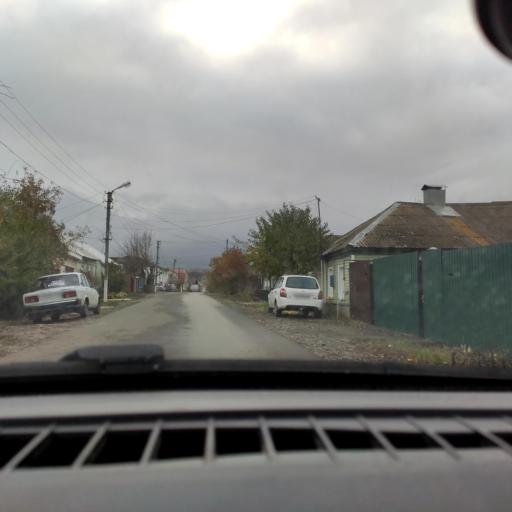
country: RU
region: Belgorod
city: Alekseyevka
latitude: 50.6287
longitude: 38.6929
